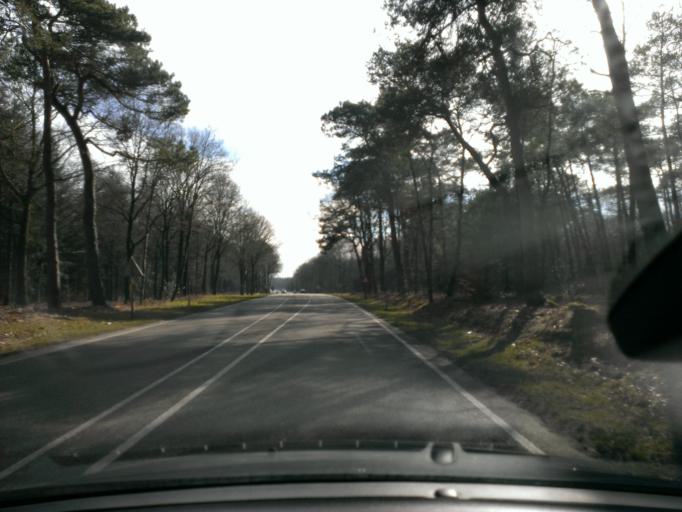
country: NL
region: Gelderland
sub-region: Gemeente Heerde
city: Heerde
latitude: 52.4174
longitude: 6.0133
